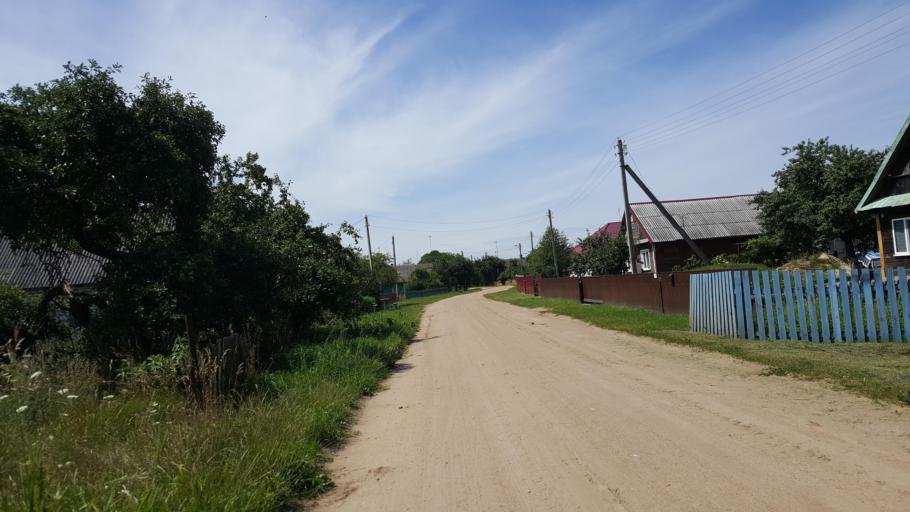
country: BY
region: Brest
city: Pruzhany
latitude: 52.5641
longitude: 24.2201
